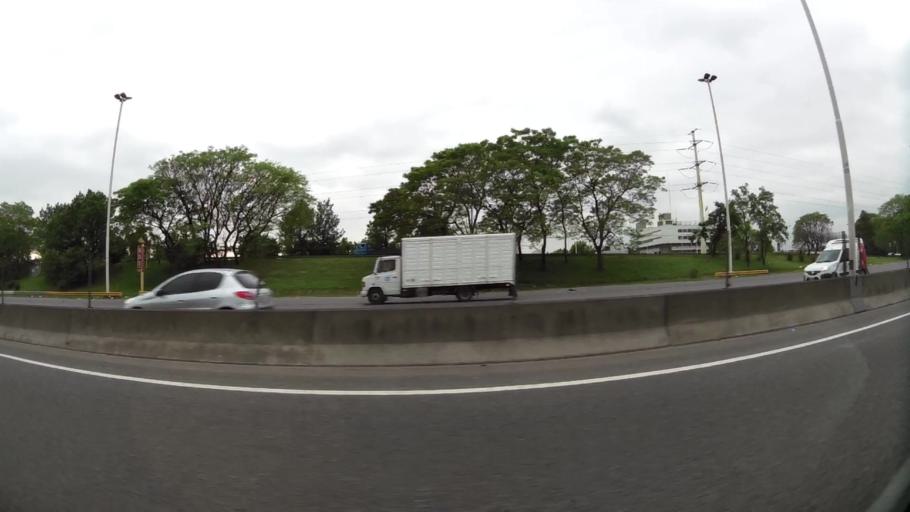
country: AR
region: Buenos Aires F.D.
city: Villa Lugano
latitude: -34.7068
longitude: -58.5018
